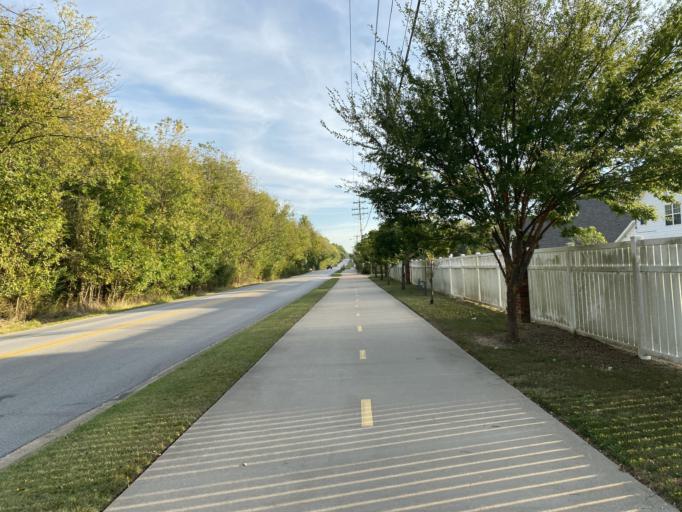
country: US
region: Arkansas
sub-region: Washington County
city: Johnson
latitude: 36.1018
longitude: -94.2080
